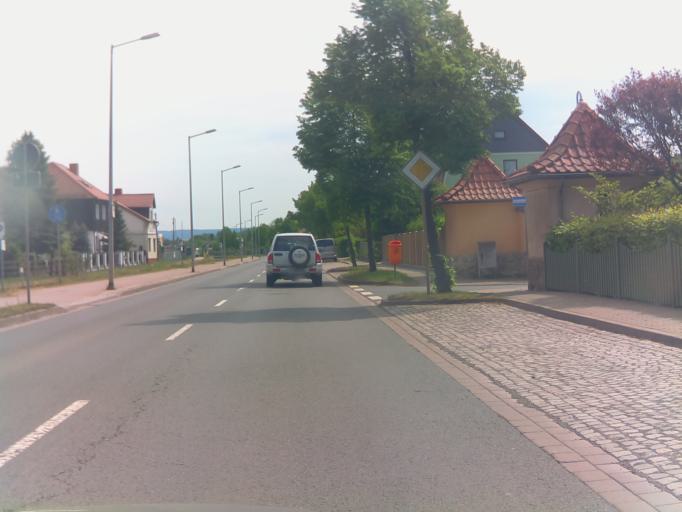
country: DE
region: Thuringia
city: Niedersachswerfen
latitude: 51.5452
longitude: 10.7687
